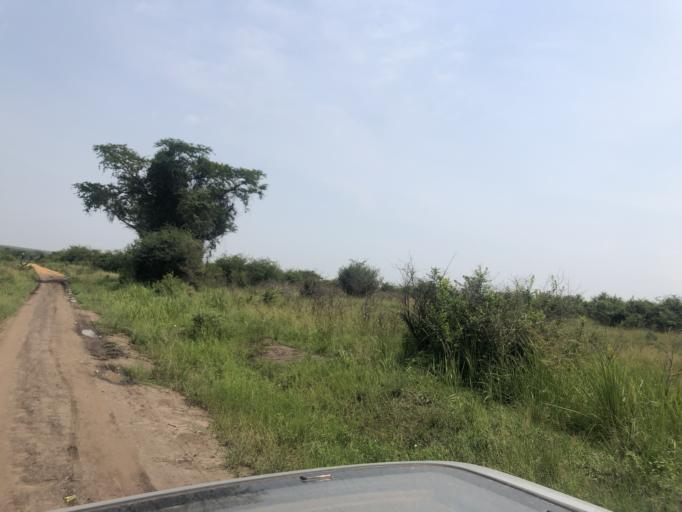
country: UG
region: Western Region
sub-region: Rubirizi District
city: Rubirizi
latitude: -0.2124
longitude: 29.9531
